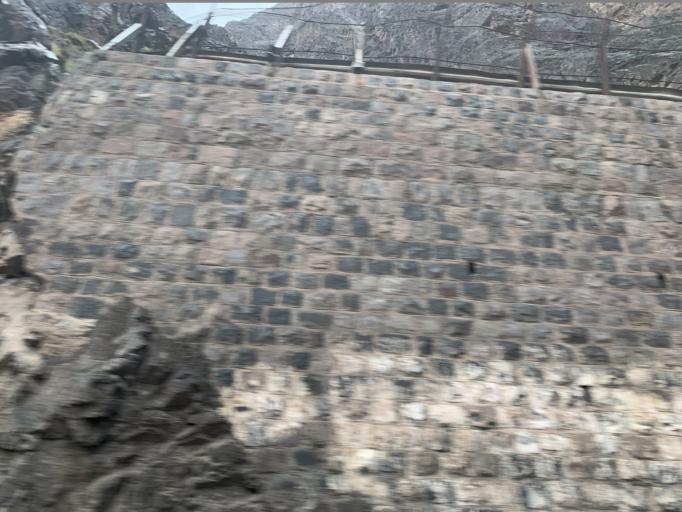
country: IR
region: Mazandaran
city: Amol
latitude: 36.1148
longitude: 52.2825
